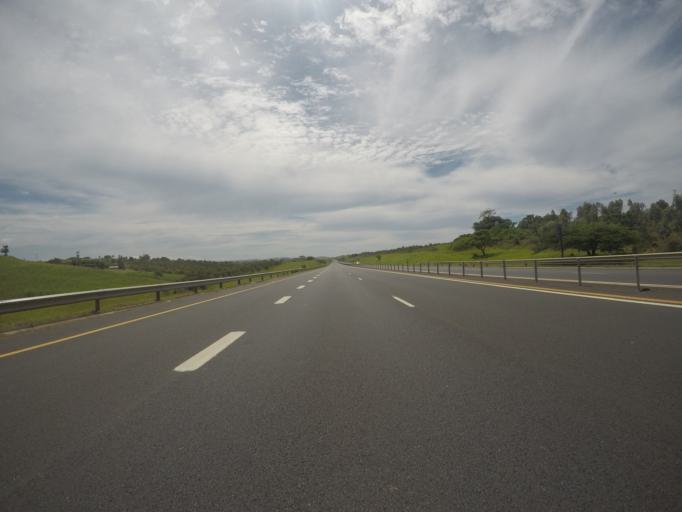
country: ZA
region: KwaZulu-Natal
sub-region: iLembe District Municipality
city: Mandeni
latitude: -29.1824
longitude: 31.4889
